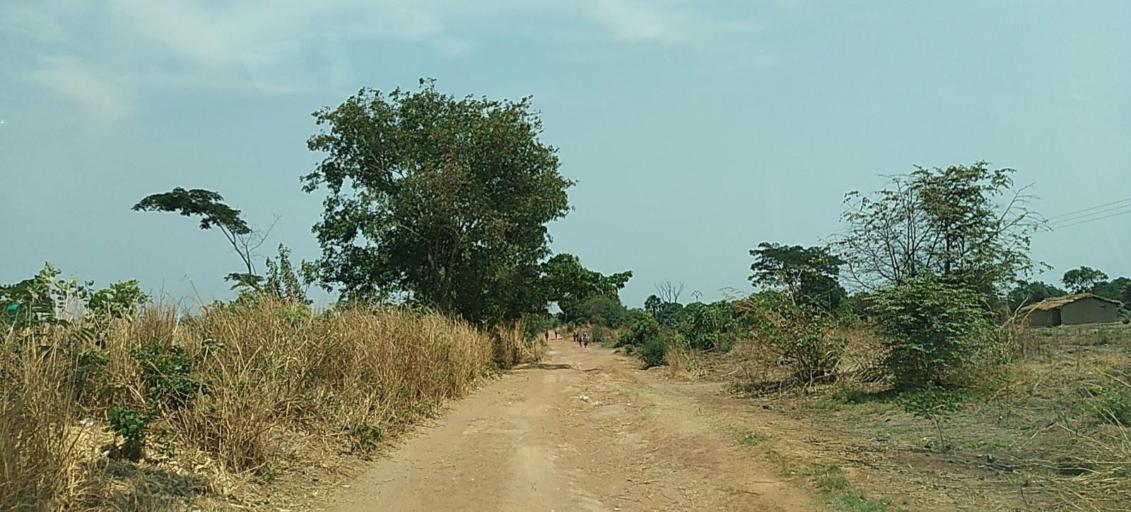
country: ZM
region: Copperbelt
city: Ndola
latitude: -13.0644
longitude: 28.7403
